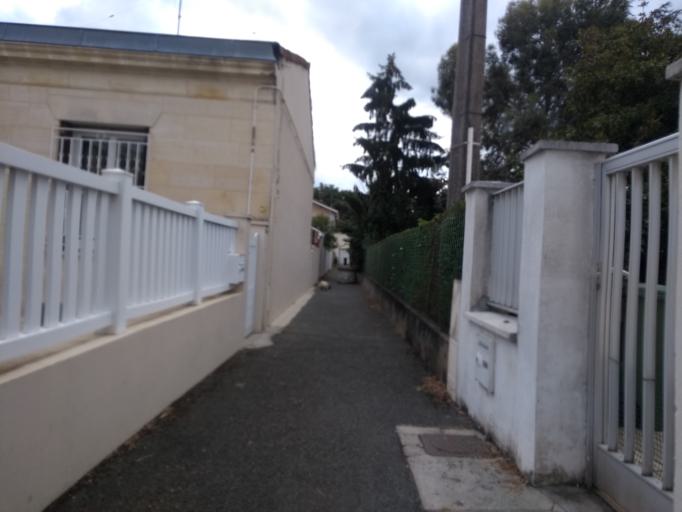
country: FR
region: Aquitaine
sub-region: Departement de la Gironde
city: Talence
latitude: 44.8098
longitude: -0.5722
